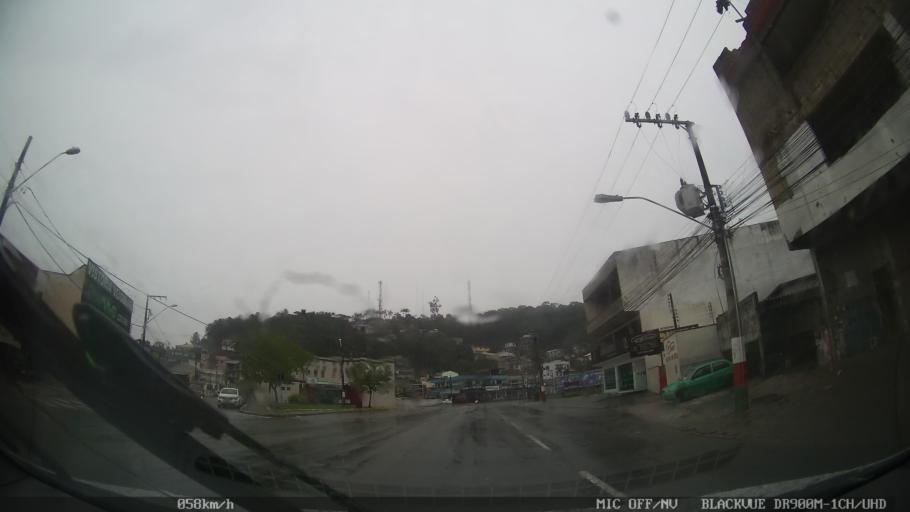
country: BR
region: Santa Catarina
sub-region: Balneario Camboriu
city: Balneario Camboriu
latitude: -27.0155
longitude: -48.6528
